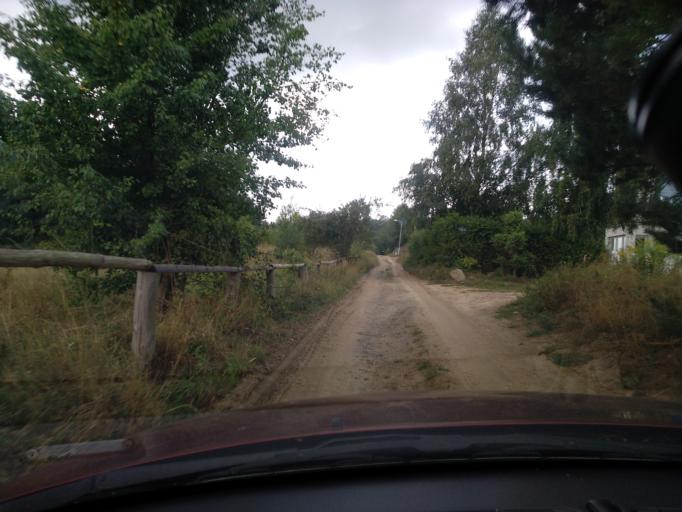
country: PL
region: West Pomeranian Voivodeship
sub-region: Powiat kamienski
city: Wolin
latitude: 53.9727
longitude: 14.5933
